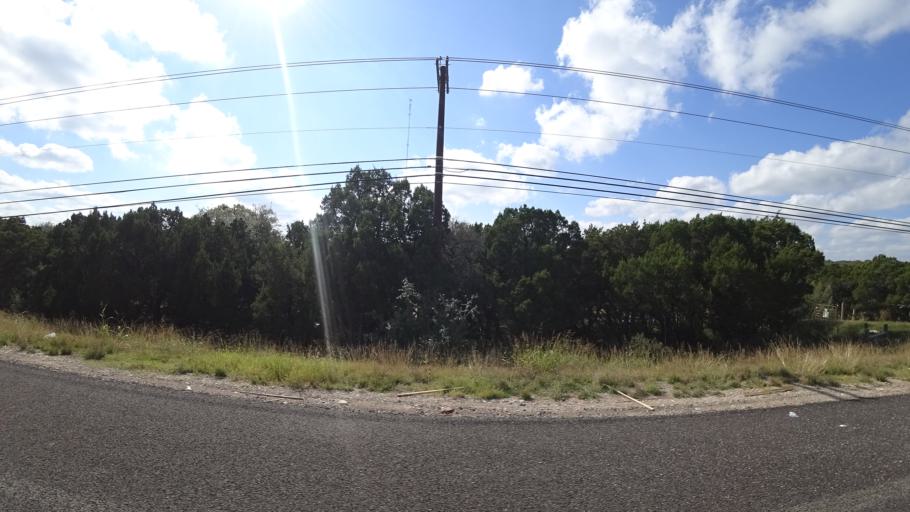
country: US
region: Texas
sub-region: Travis County
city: Barton Creek
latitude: 30.2526
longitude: -97.8998
